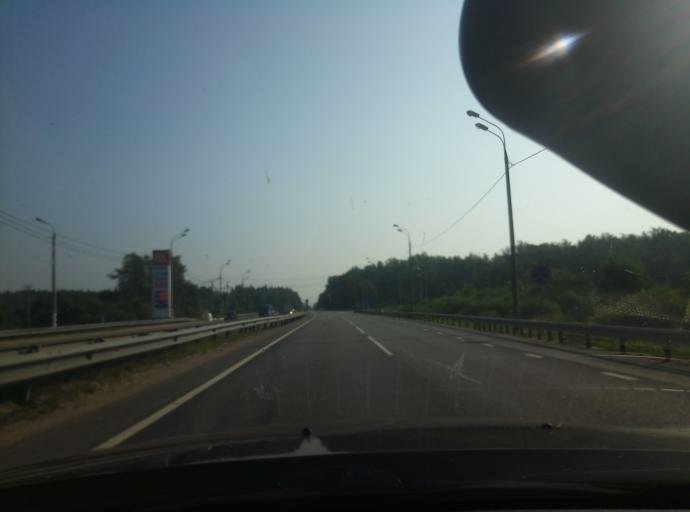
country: RU
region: Kaluga
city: Maloyaroslavets
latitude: 54.9820
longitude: 36.4979
